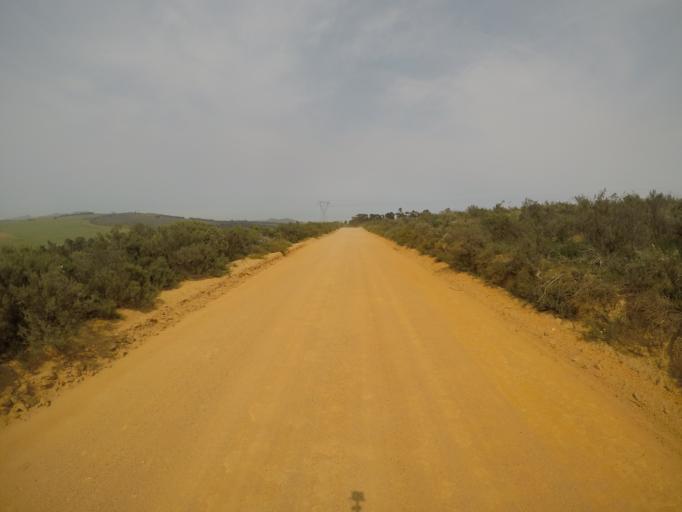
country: ZA
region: Western Cape
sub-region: West Coast District Municipality
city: Malmesbury
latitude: -33.4520
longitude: 18.7442
